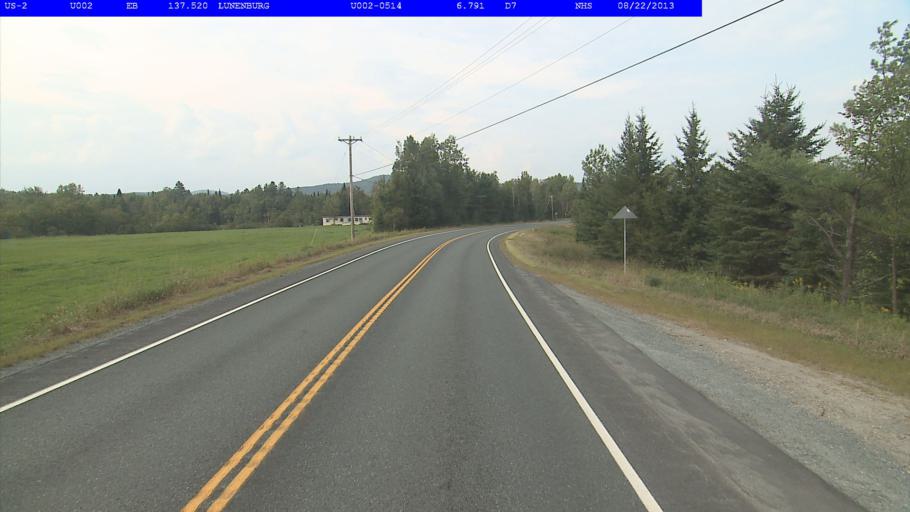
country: US
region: New Hampshire
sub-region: Coos County
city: Lancaster
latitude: 44.4735
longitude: -71.6480
